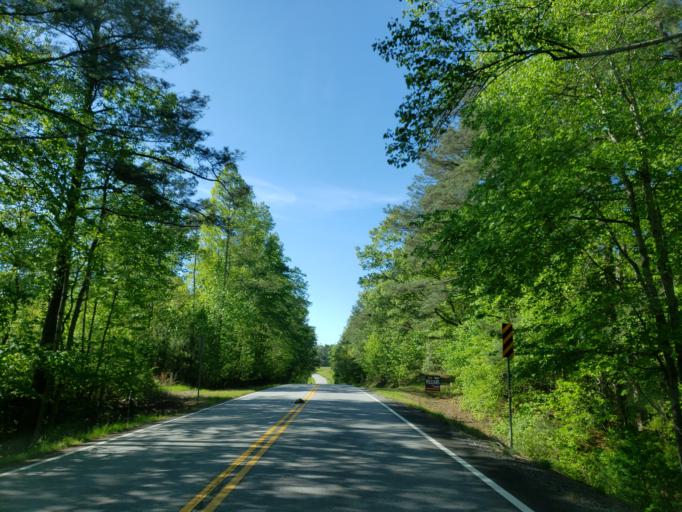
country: US
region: Georgia
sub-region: Haralson County
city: Tallapoosa
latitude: 33.8593
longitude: -85.2920
